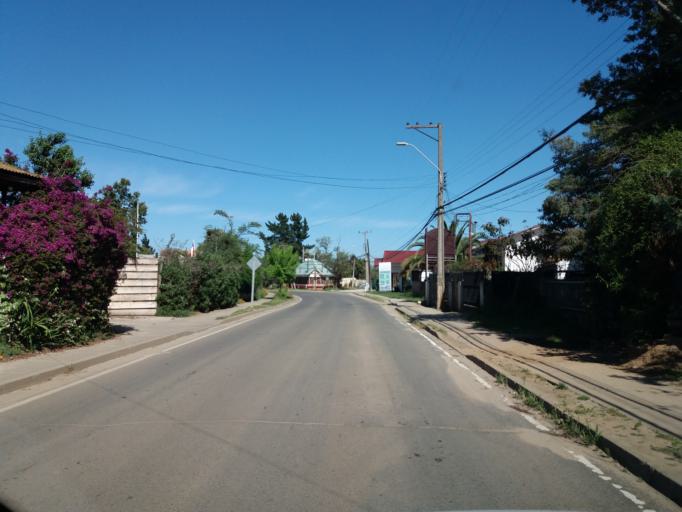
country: CL
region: Valparaiso
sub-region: Provincia de Marga Marga
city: Limache
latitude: -32.9924
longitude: -71.1665
